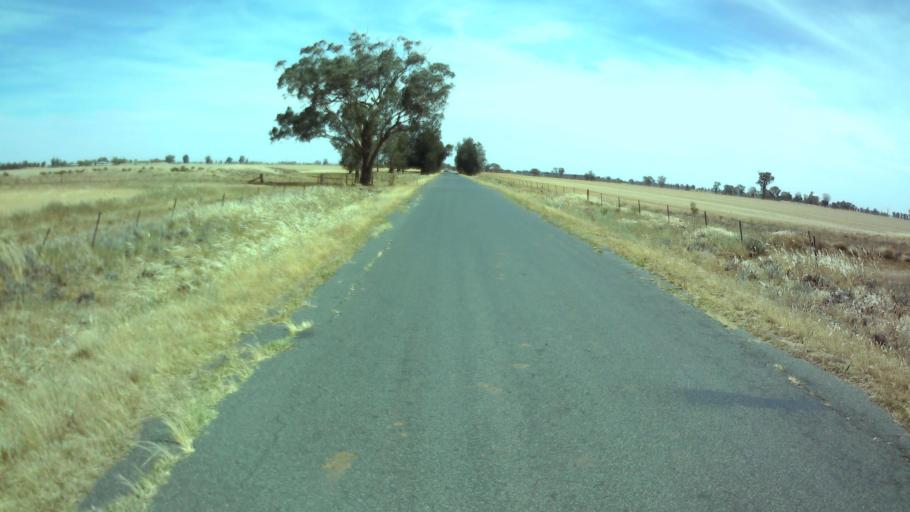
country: AU
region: New South Wales
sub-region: Weddin
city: Grenfell
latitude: -33.9269
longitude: 147.7631
